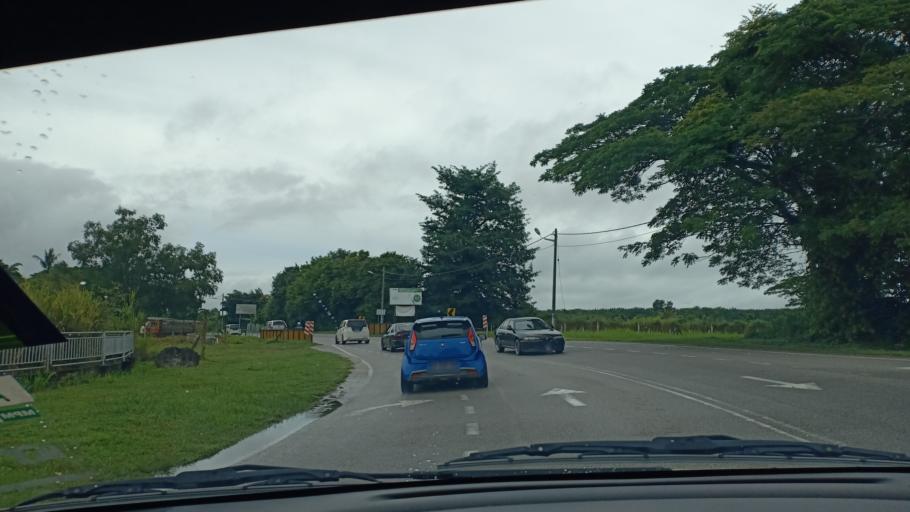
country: MY
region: Penang
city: Kepala Batas
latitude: 5.4919
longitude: 100.4572
